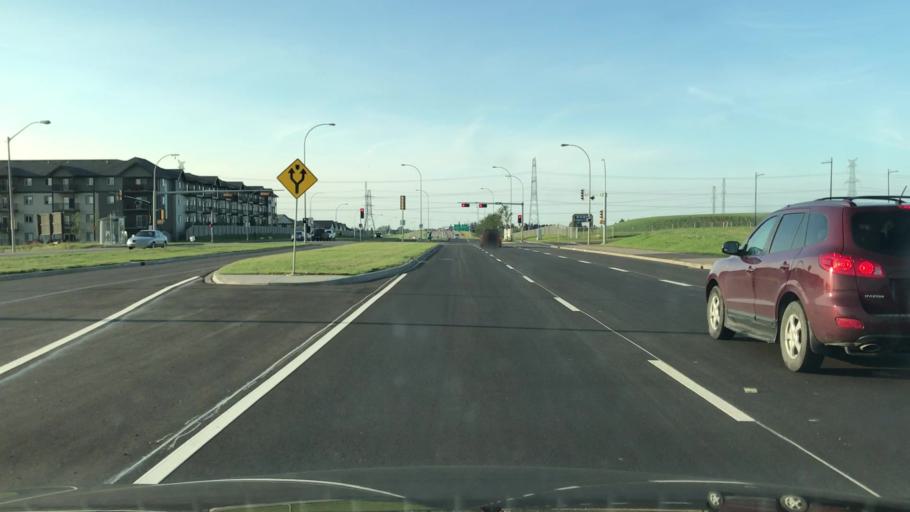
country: CA
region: Alberta
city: Beaumont
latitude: 53.4274
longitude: -113.4178
